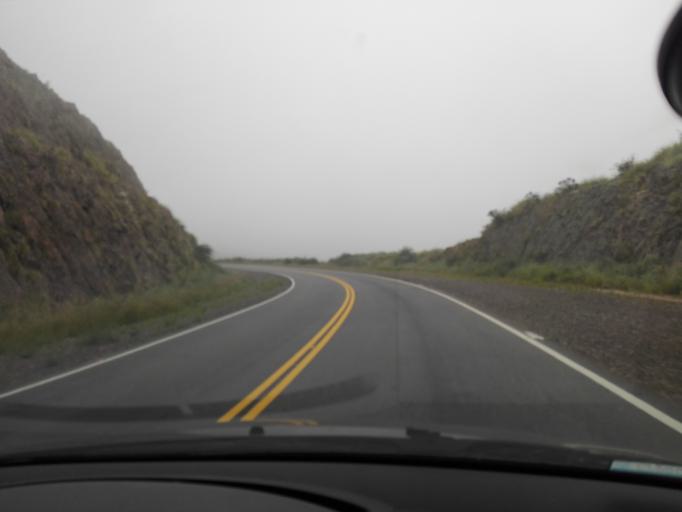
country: AR
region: Cordoba
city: Cuesta Blanca
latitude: -31.6015
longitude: -64.6983
